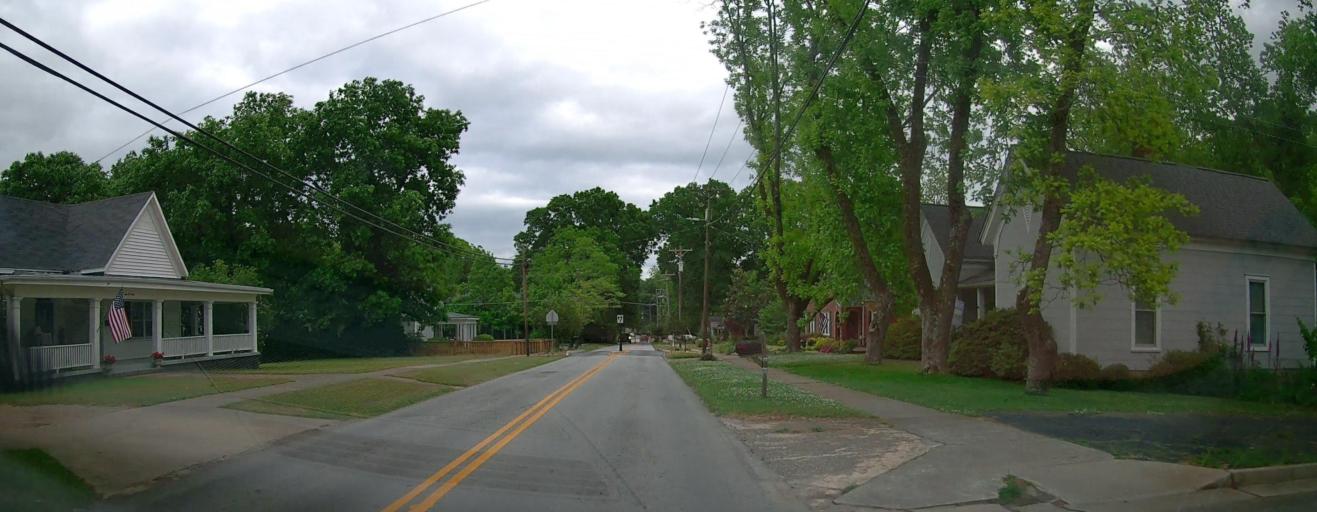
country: US
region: Georgia
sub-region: Walton County
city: Monroe
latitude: 33.7926
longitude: -83.7057
